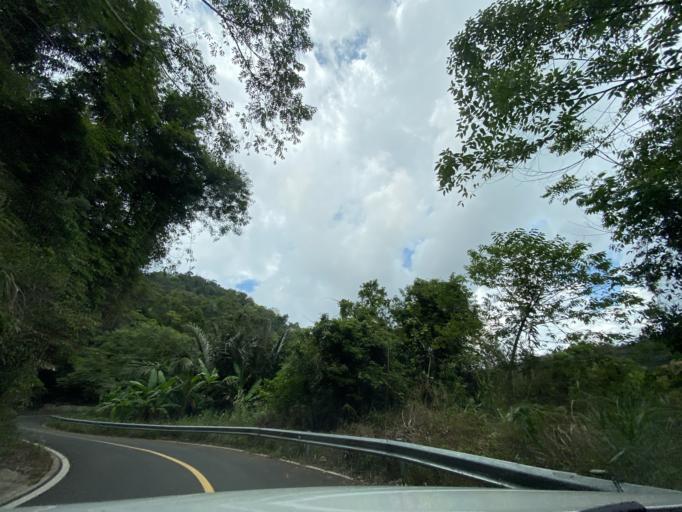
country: CN
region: Hainan
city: Benhao
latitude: 18.6877
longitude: 109.8783
